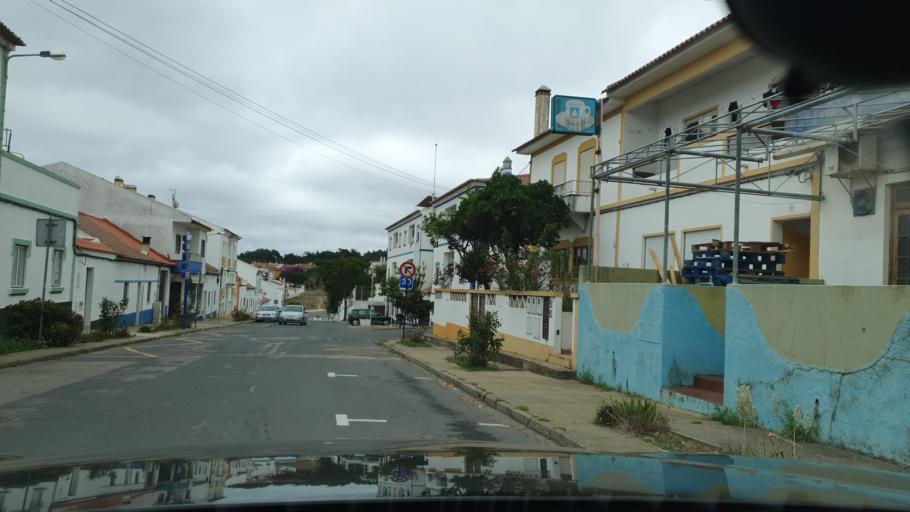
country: PT
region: Beja
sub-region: Odemira
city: Sao Teotonio
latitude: 37.5120
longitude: -8.7031
